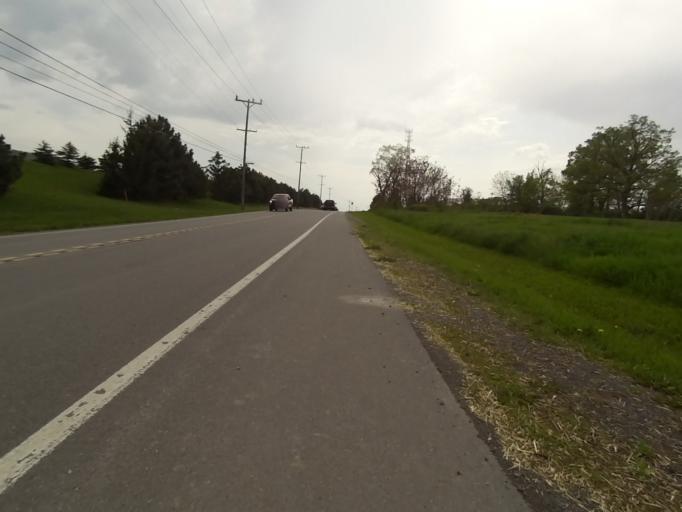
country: US
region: Pennsylvania
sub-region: Centre County
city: Pleasant Gap
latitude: 40.8837
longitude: -77.7162
